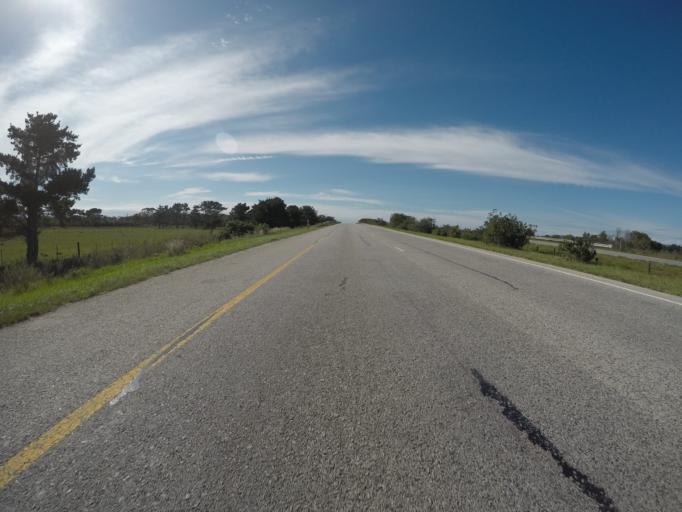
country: ZA
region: Eastern Cape
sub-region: Nelson Mandela Bay Metropolitan Municipality
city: Port Elizabeth
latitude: -33.9493
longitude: 25.4387
